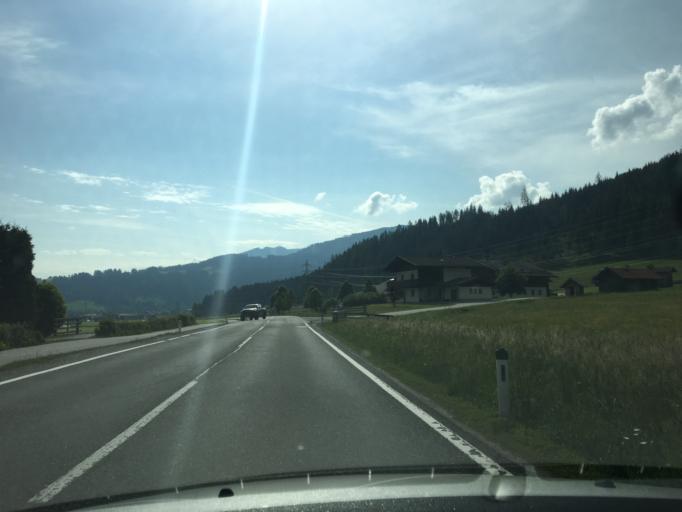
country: AT
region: Salzburg
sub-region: Politischer Bezirk Sankt Johann im Pongau
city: Flachau
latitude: 47.3596
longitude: 13.3652
